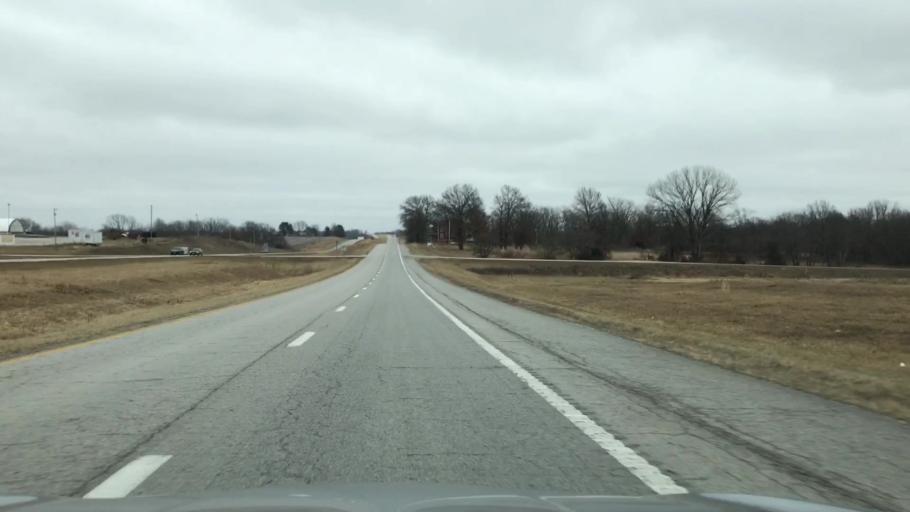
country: US
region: Missouri
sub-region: Linn County
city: Brookfield
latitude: 39.7784
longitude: -93.1678
